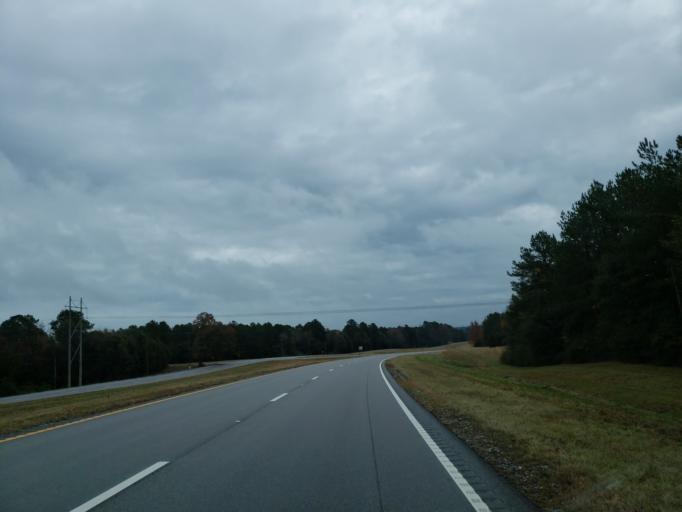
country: US
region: Mississippi
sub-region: Wayne County
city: Waynesboro
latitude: 31.6960
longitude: -88.7257
